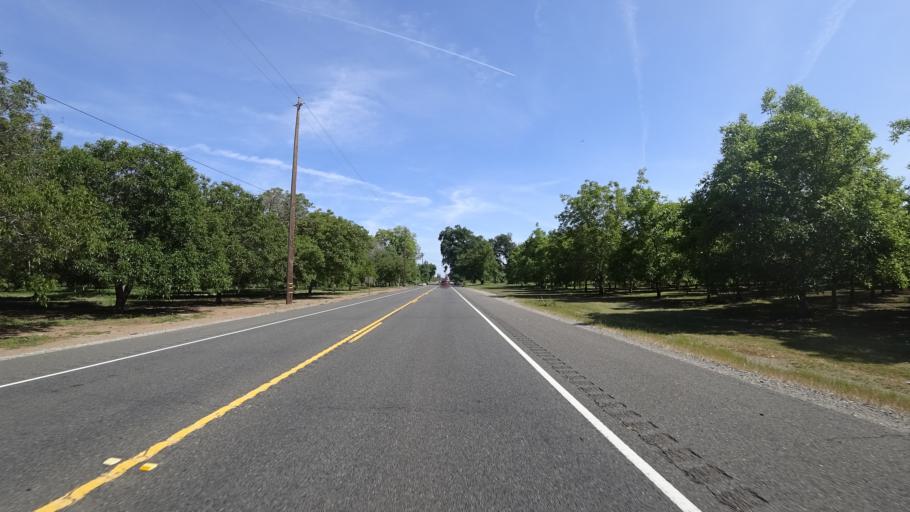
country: US
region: California
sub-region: Tehama County
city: Red Bluff
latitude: 40.1653
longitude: -122.1547
